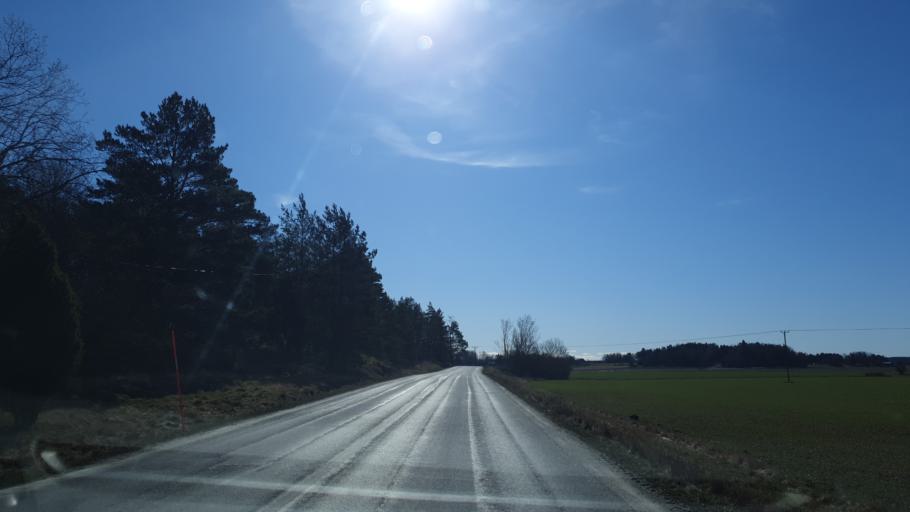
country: SE
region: Uppsala
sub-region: Enkopings Kommun
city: Grillby
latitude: 59.6066
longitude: 17.2754
